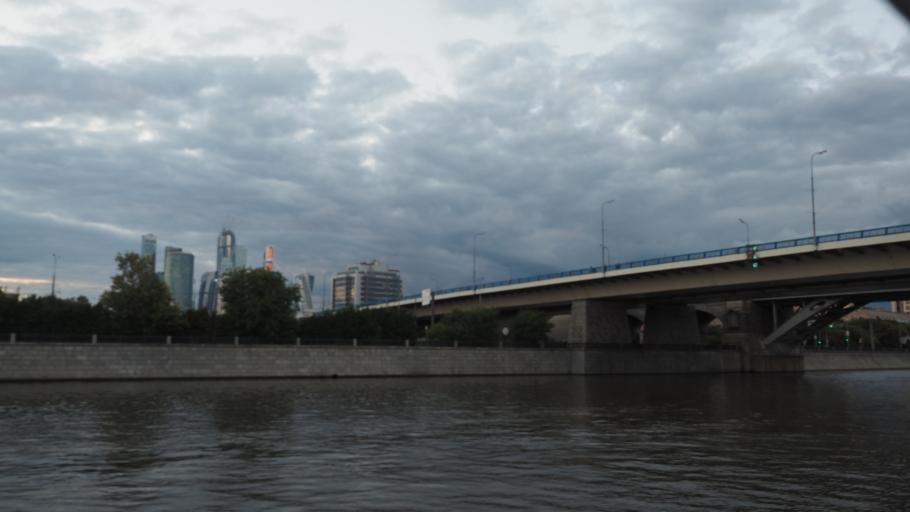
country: RU
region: Moscow
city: Luzhniki
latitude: 55.7271
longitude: 37.5458
